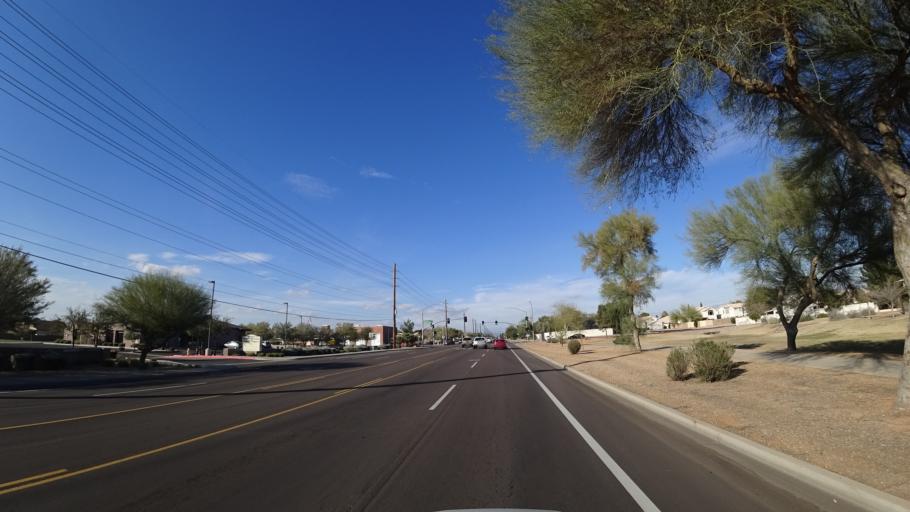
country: US
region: Arizona
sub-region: Maricopa County
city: Peoria
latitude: 33.6053
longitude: -112.2376
